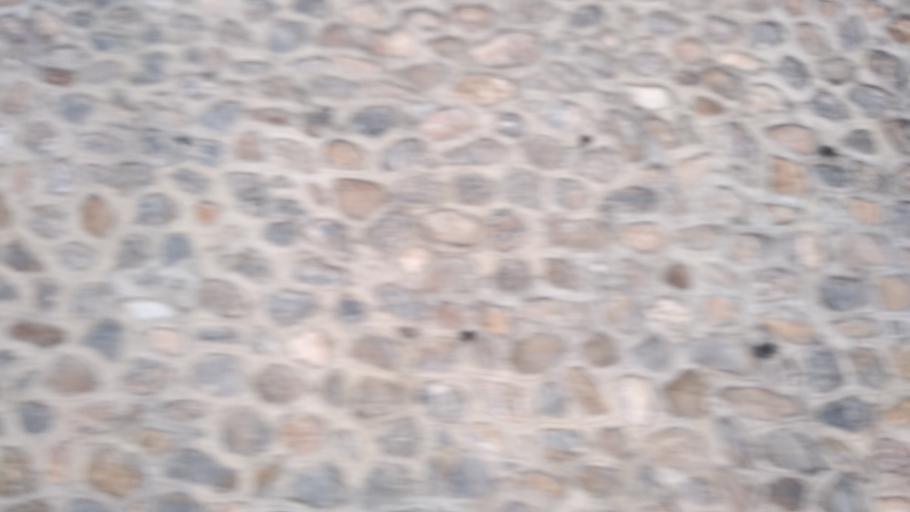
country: TR
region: Bitlis
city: Resadiye
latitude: 38.4782
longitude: 42.5366
